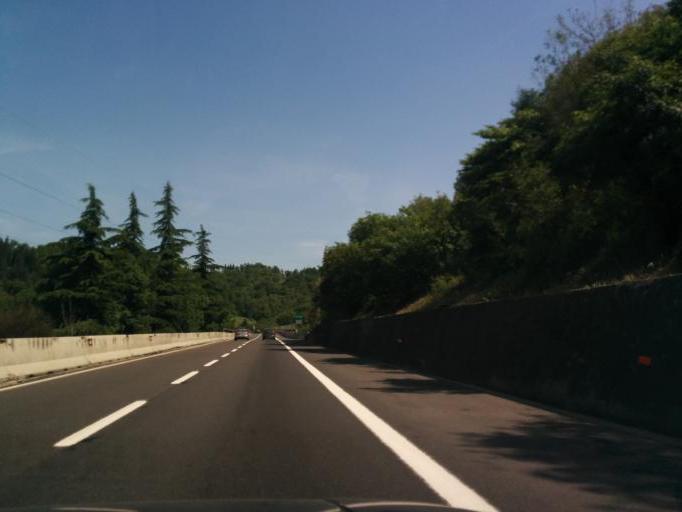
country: IT
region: Tuscany
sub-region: Province of Florence
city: Cavallina
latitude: 43.9374
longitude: 11.2221
